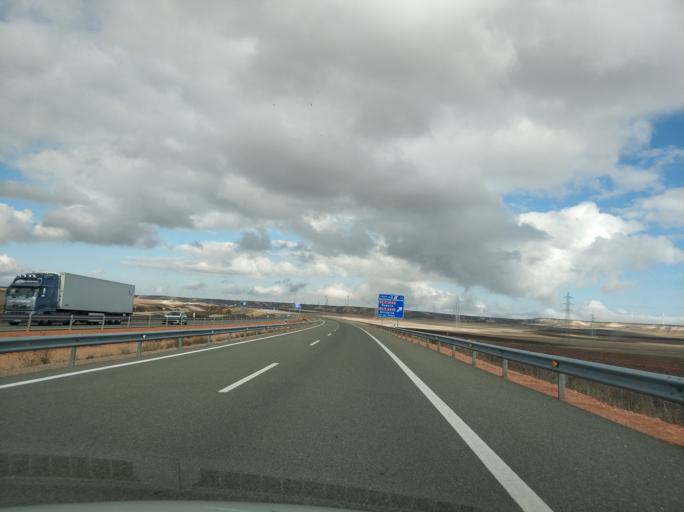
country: ES
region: Castille and Leon
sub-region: Provincia de Soria
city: Yelo
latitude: 41.2458
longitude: -2.4759
